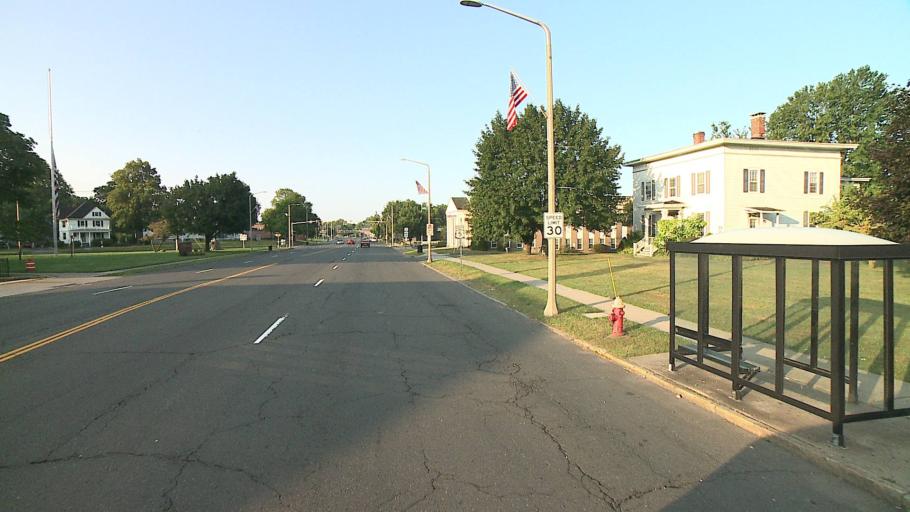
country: US
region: Connecticut
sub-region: Hartford County
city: East Hartford
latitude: 41.7688
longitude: -72.6442
